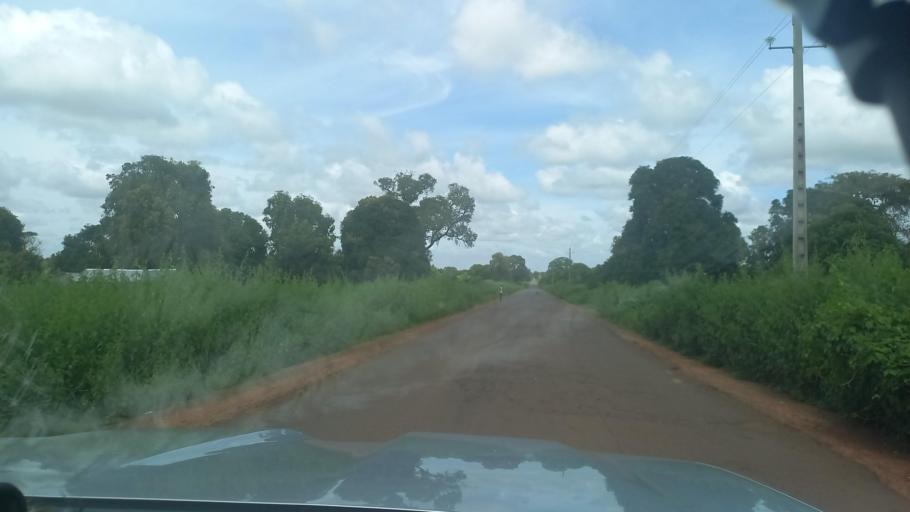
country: GM
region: Lower River
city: Kaiaf
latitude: 13.2287
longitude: -15.5374
